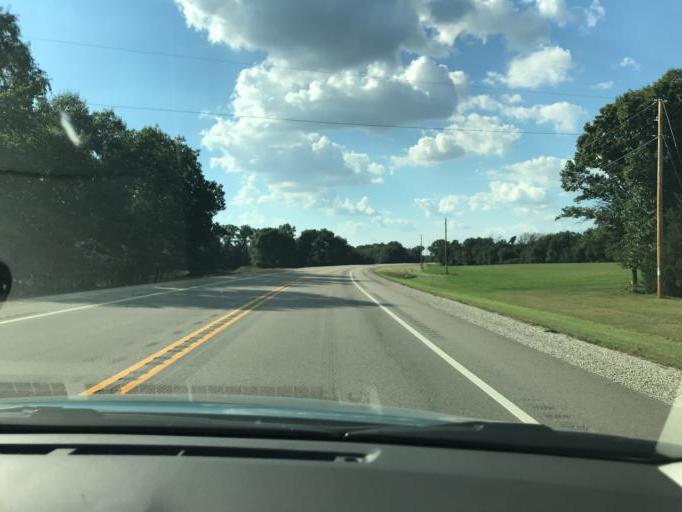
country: US
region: Wisconsin
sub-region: Green County
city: Brodhead
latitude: 42.5756
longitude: -89.3709
